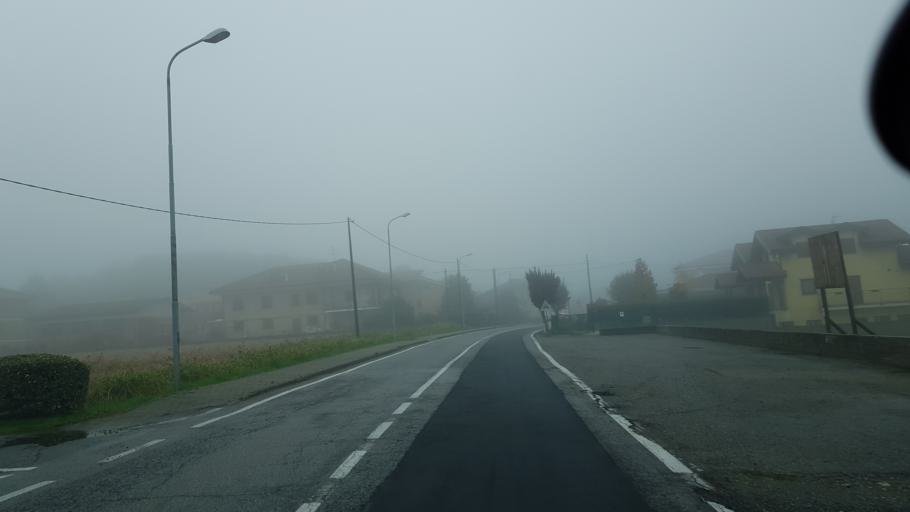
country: IT
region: Piedmont
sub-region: Provincia di Cuneo
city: Villafalletto
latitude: 44.5485
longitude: 7.5438
